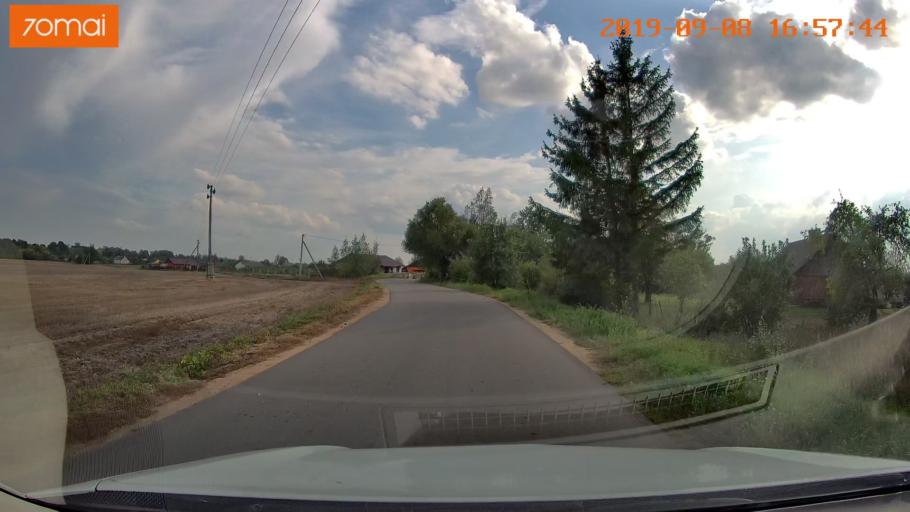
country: BY
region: Grodnenskaya
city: Hrodna
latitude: 53.7302
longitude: 23.9273
